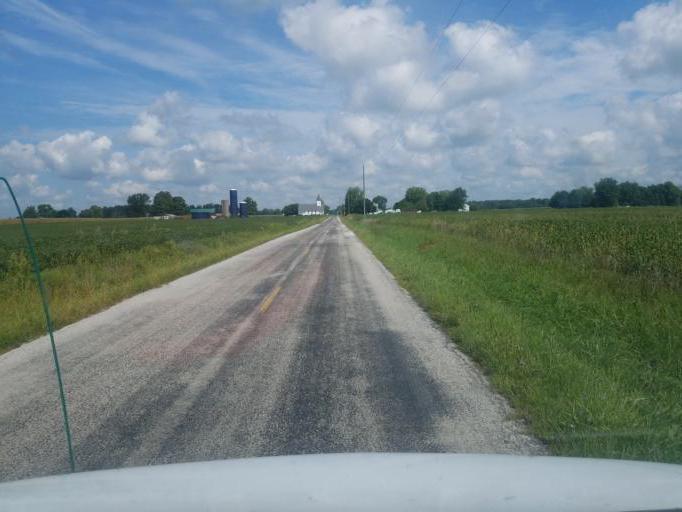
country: US
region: Ohio
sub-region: Marion County
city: Prospect
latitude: 40.4939
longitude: -83.1315
